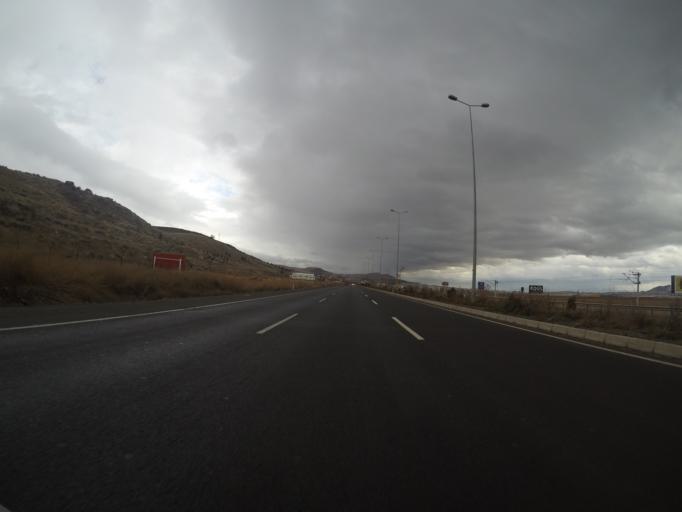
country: TR
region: Kayseri
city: Melikgazi
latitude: 38.7439
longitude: 35.3001
